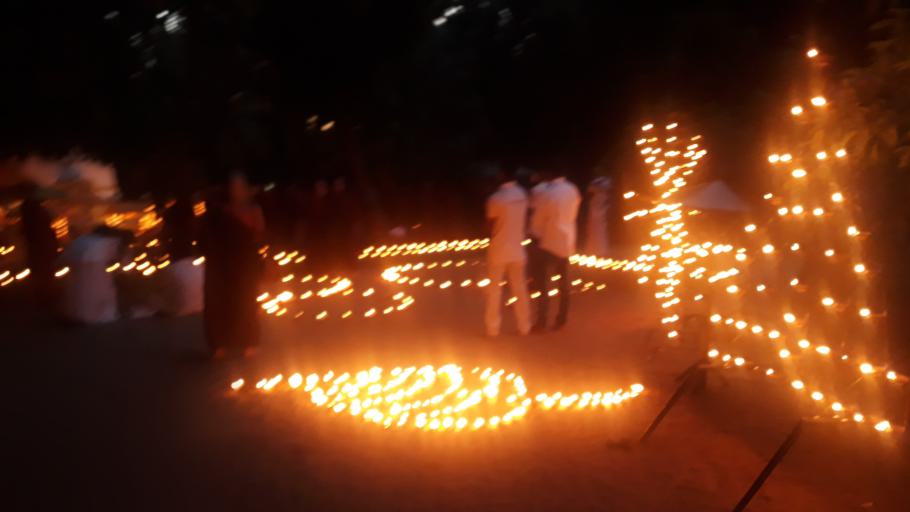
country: LK
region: Central
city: Dambulla
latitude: 7.7388
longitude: 80.5187
